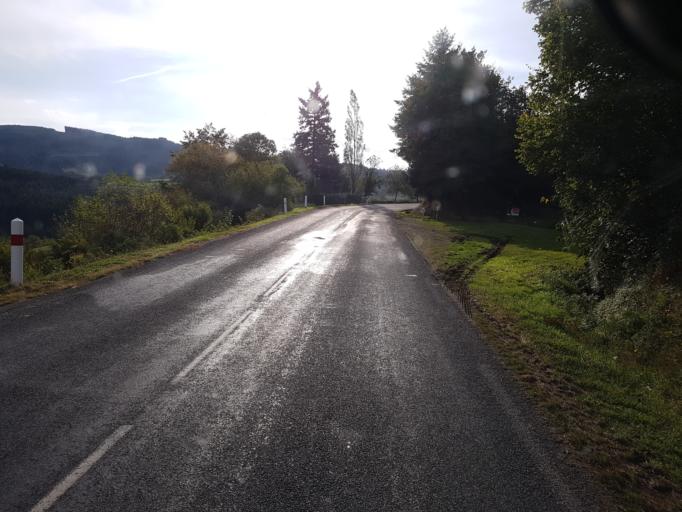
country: FR
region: Rhone-Alpes
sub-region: Departement de la Loire
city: Belmont-de-la-Loire
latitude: 46.2031
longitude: 4.4441
